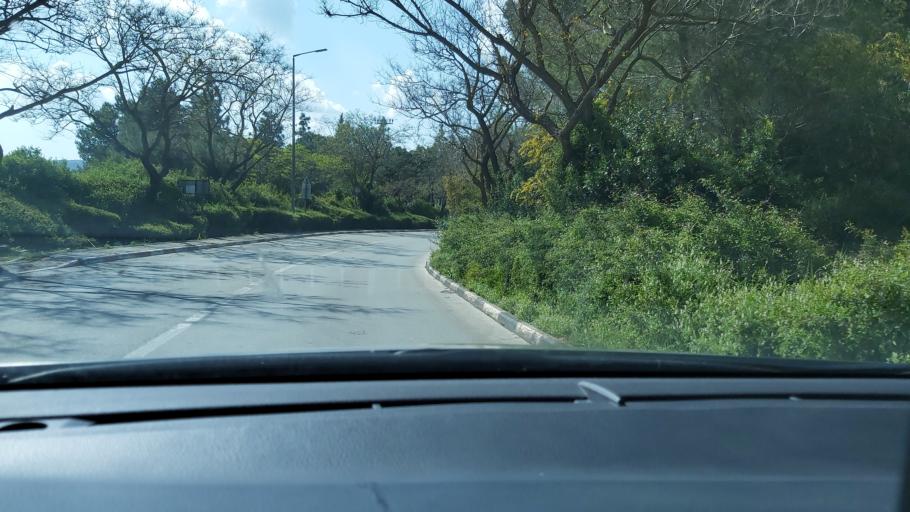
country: IL
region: Jerusalem
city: Ariel
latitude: 32.1014
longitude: 35.1665
